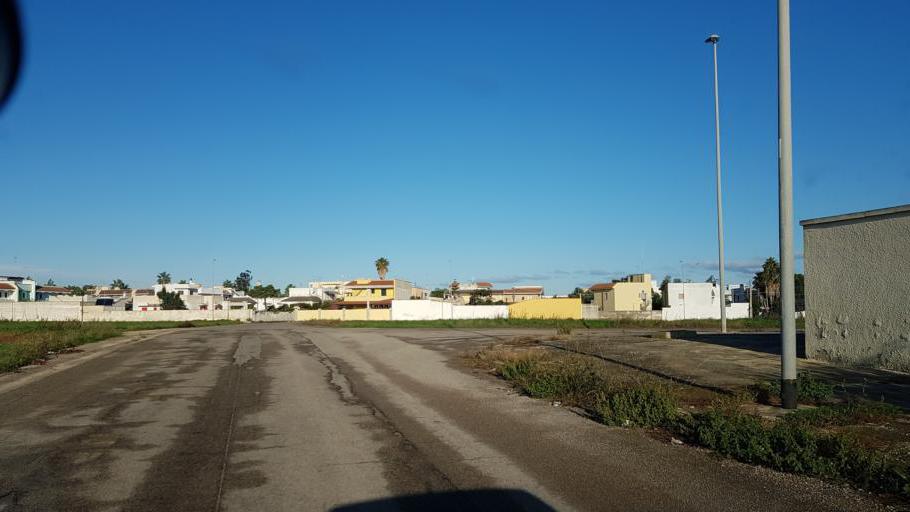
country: IT
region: Apulia
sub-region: Provincia di Brindisi
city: Torchiarolo
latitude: 40.5370
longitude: 18.0698
